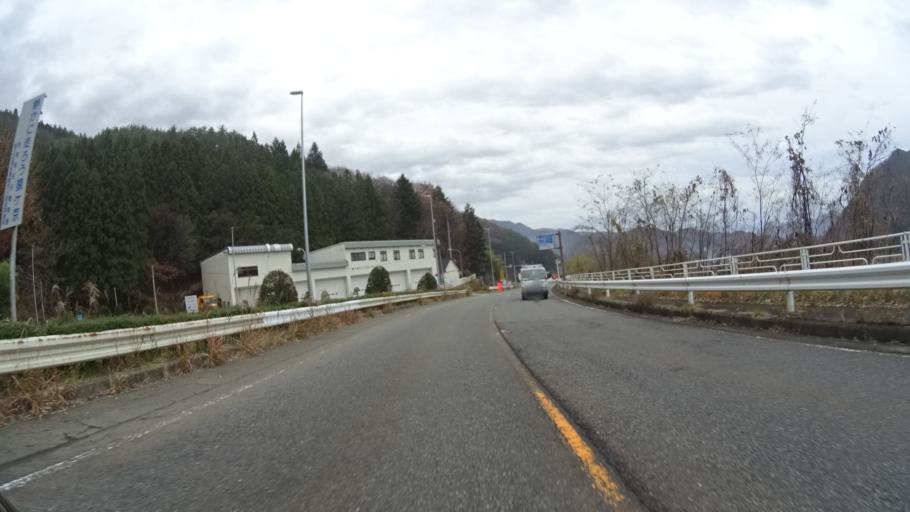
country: JP
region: Gunma
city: Nakanojomachi
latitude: 36.7299
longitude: 138.8762
